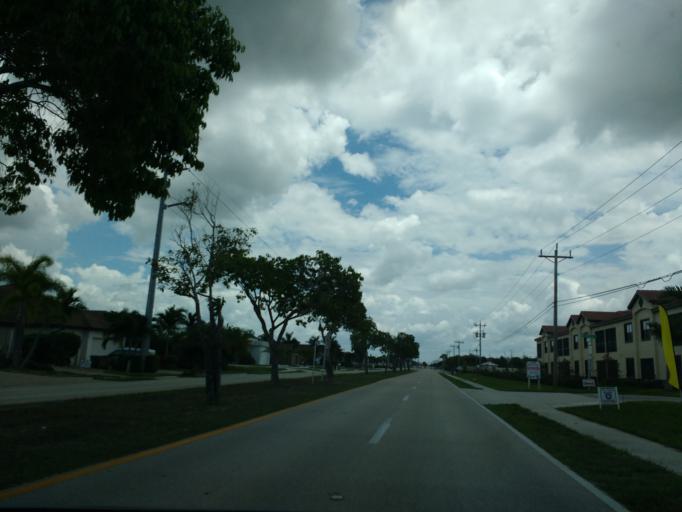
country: US
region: Florida
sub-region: Lee County
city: Cape Coral
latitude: 26.5627
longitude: -82.0131
